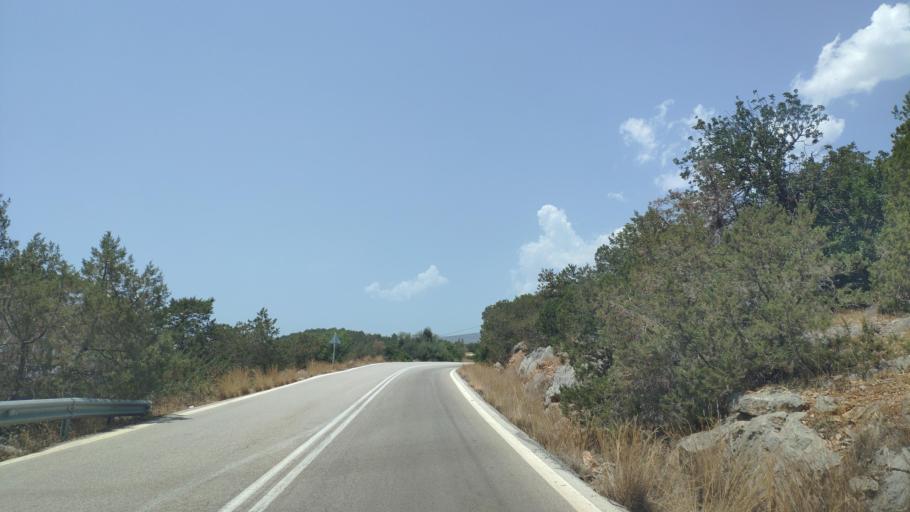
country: GR
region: Peloponnese
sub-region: Nomos Argolidos
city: Koilas
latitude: 37.4219
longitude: 23.1537
